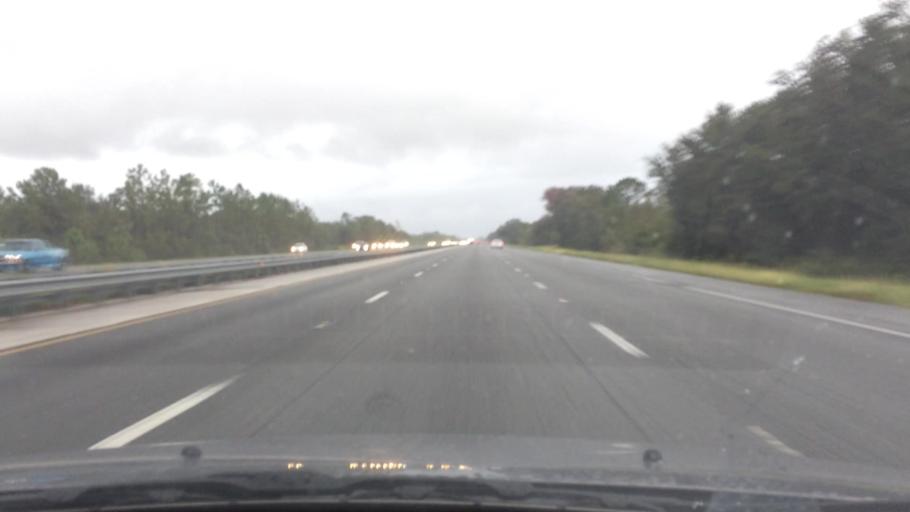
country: US
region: Florida
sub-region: Volusia County
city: Ormond-by-the-Sea
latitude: 29.3104
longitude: -81.1316
